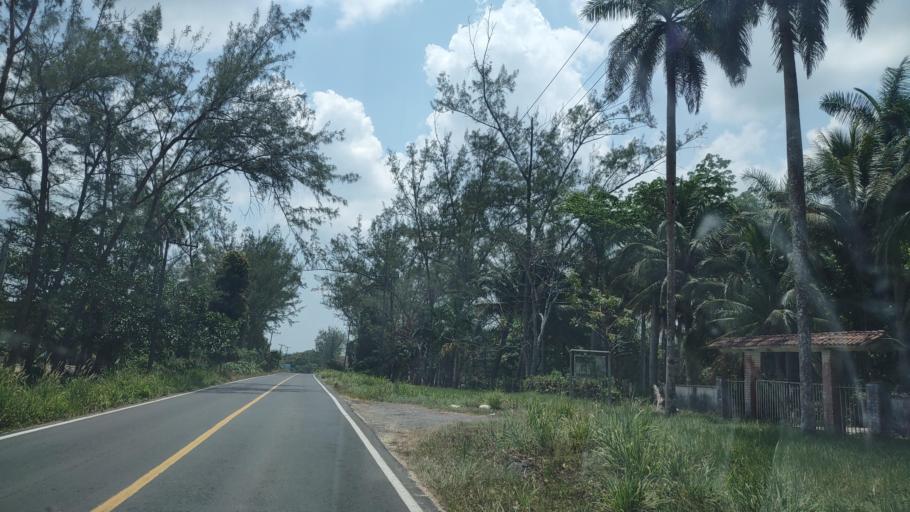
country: MX
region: Veracruz
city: Las Choapas
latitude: 17.9270
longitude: -94.1415
